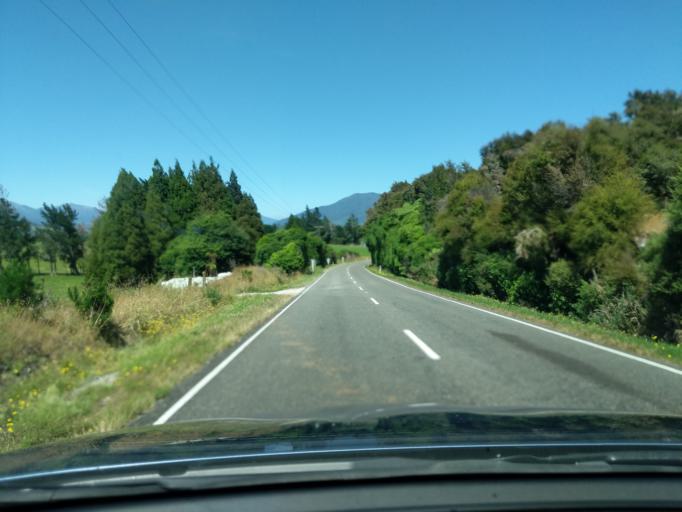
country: NZ
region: Tasman
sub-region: Tasman District
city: Takaka
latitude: -40.6930
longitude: 172.6411
